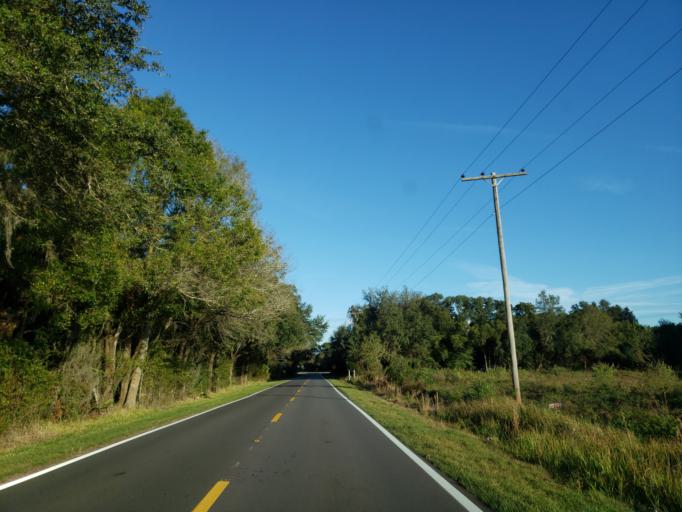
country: US
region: Florida
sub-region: Hillsborough County
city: Boyette
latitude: 27.8176
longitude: -82.2257
